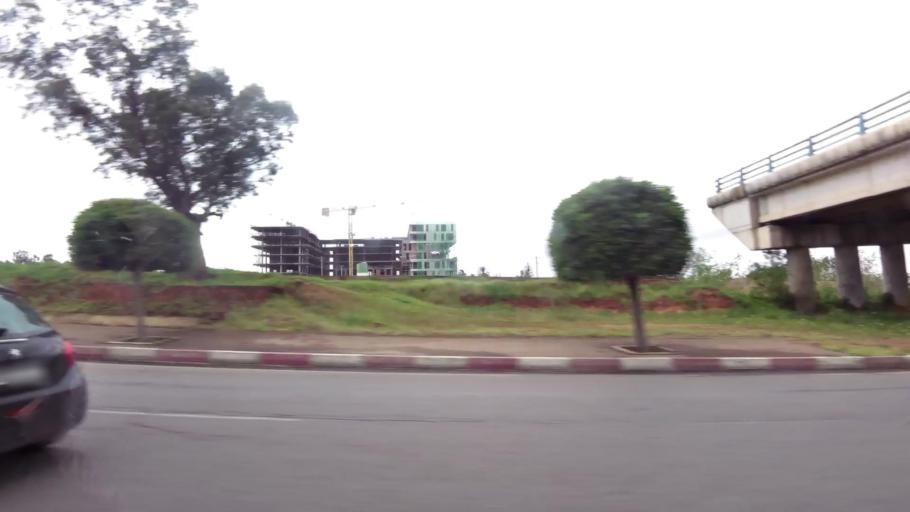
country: MA
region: Grand Casablanca
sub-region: Nouaceur
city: Bouskoura
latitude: 33.5115
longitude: -7.6307
